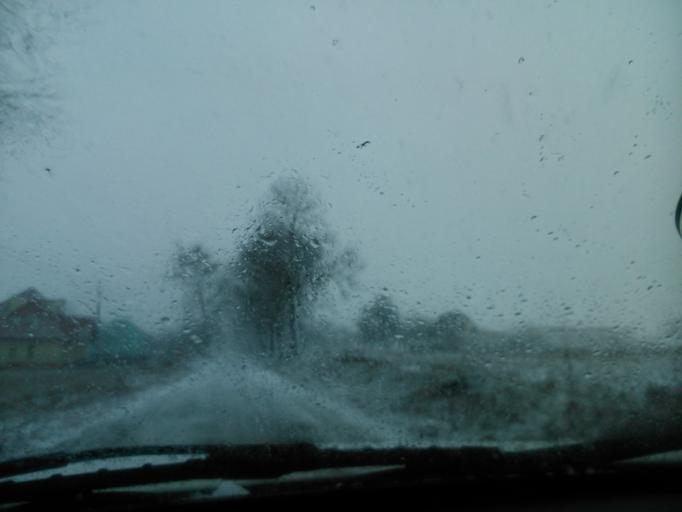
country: PL
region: Kujawsko-Pomorskie
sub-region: Powiat wabrzeski
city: Debowa Laka
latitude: 53.2082
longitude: 19.1691
